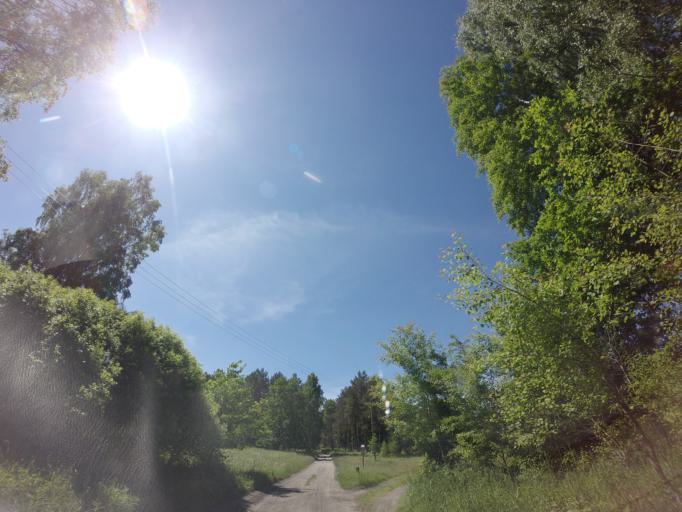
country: PL
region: West Pomeranian Voivodeship
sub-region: Powiat choszczenski
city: Drawno
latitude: 53.3141
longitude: 15.6912
